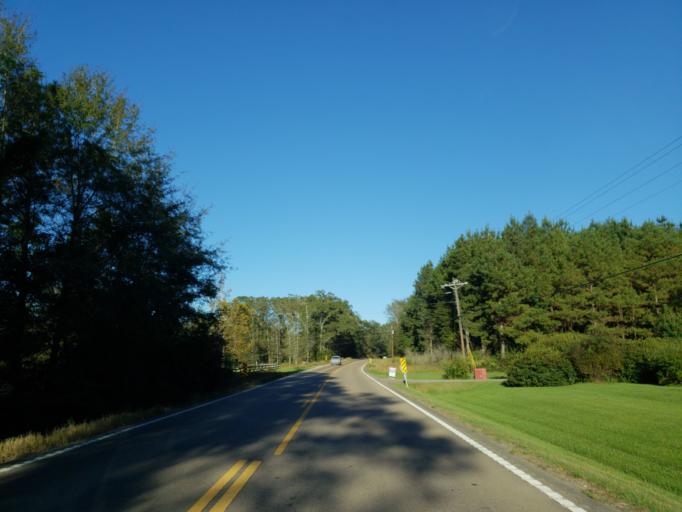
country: US
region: Mississippi
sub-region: Perry County
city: Richton
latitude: 31.3739
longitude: -88.8644
